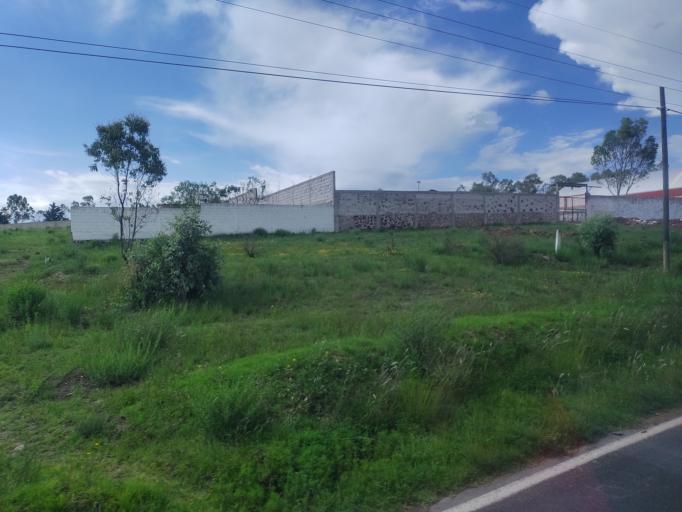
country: MX
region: Mexico
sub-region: Aculco
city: El Colorado
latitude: 20.0920
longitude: -99.7727
